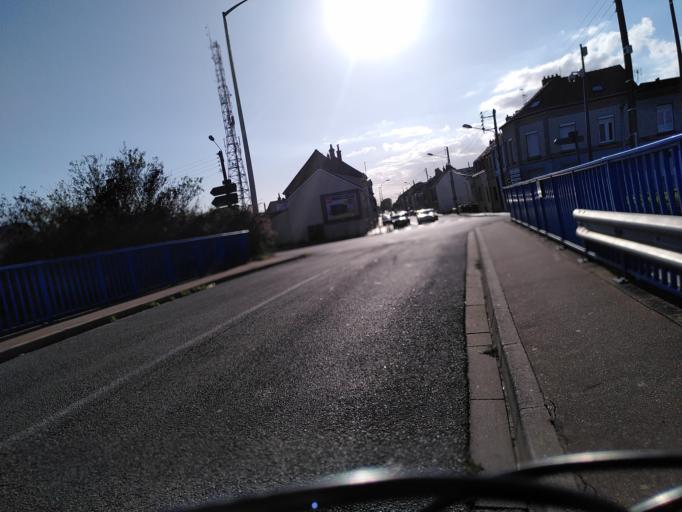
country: FR
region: Nord-Pas-de-Calais
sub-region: Departement du Pas-de-Calais
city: Calais
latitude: 50.9580
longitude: 1.8753
